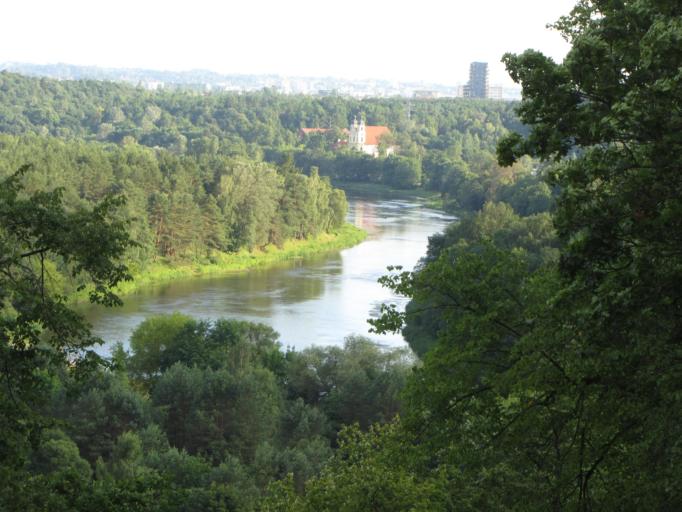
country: LT
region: Vilnius County
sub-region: Vilnius
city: Fabijoniskes
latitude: 54.7469
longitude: 25.2924
